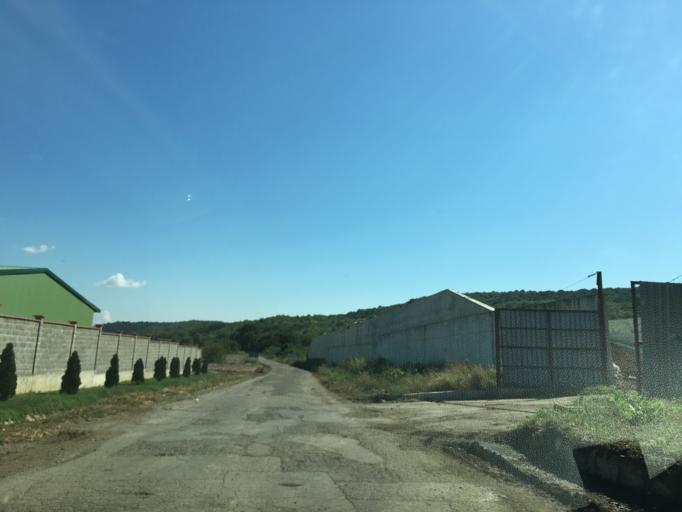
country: RO
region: Dolj
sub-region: Comuna Desa
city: Desa
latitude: 43.7648
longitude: 23.0186
